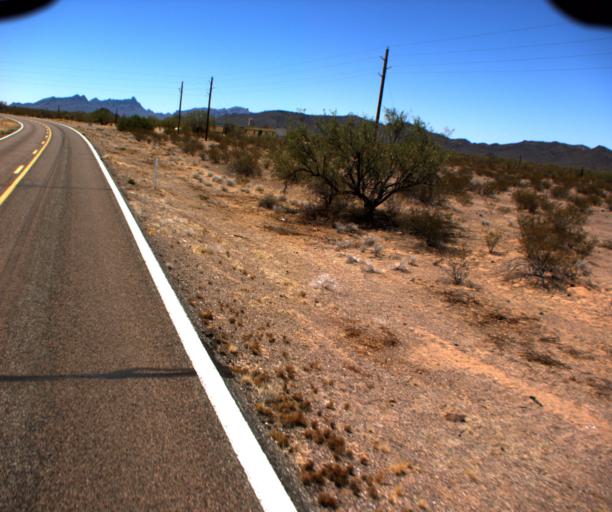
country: US
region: Arizona
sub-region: Pima County
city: Ajo
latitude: 32.2455
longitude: -112.7284
